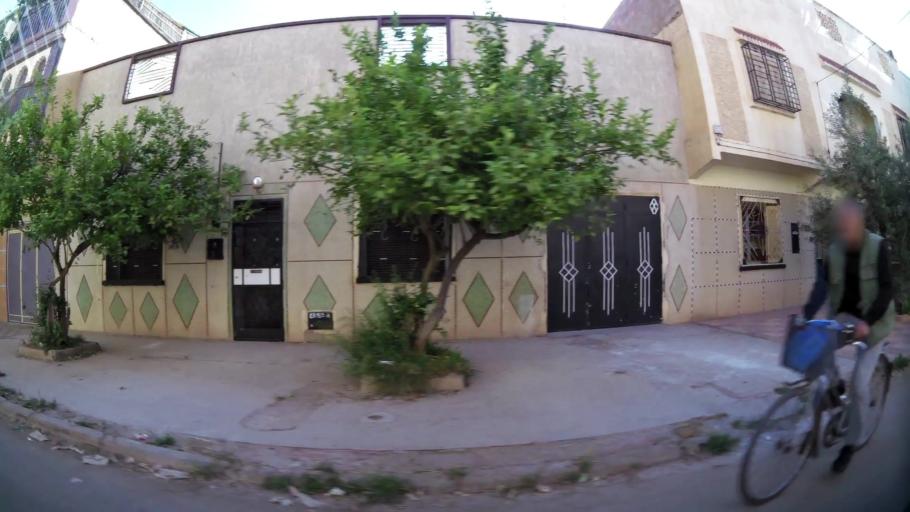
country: MA
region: Oriental
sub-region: Oujda-Angad
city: Oujda
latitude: 34.6740
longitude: -1.8986
